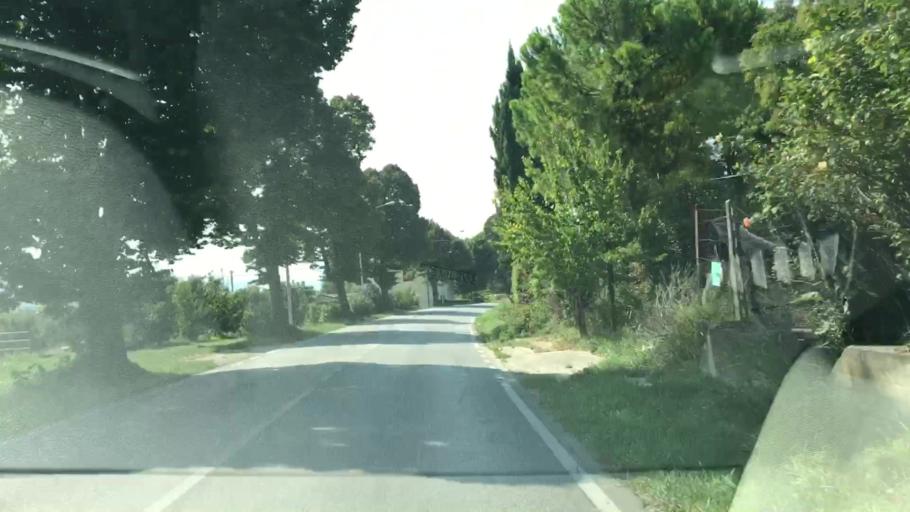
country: IT
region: The Marches
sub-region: Provincia di Ascoli Piceno
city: Pagliare
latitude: 42.8759
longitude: 13.7759
